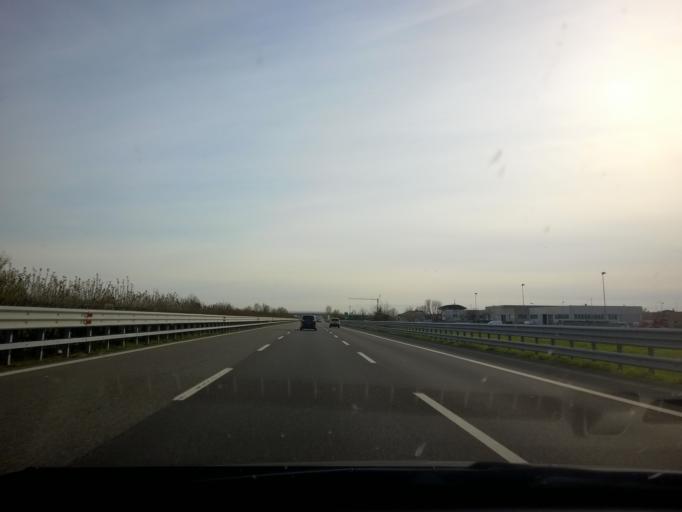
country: IT
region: Lombardy
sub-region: Provincia di Brescia
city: Bagnolo Mella
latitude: 45.4204
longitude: 10.1976
